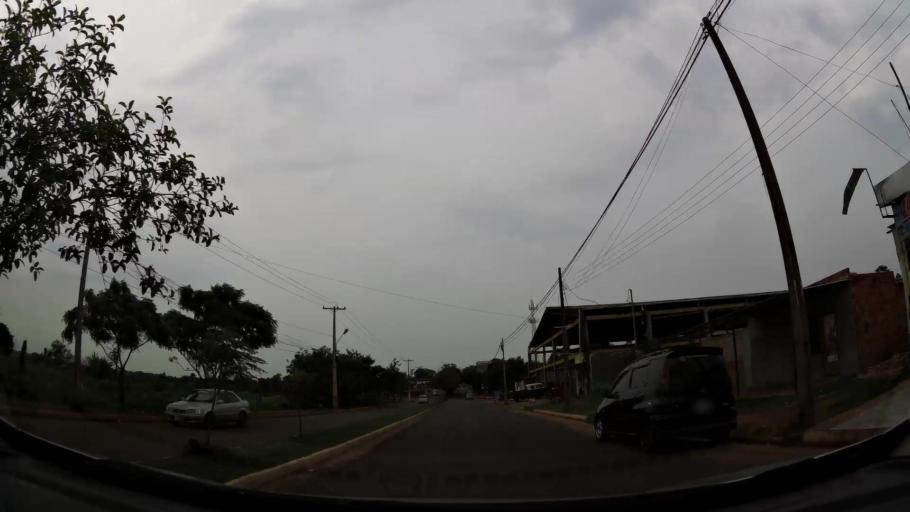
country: PY
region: Alto Parana
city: Presidente Franco
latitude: -25.5230
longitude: -54.6454
